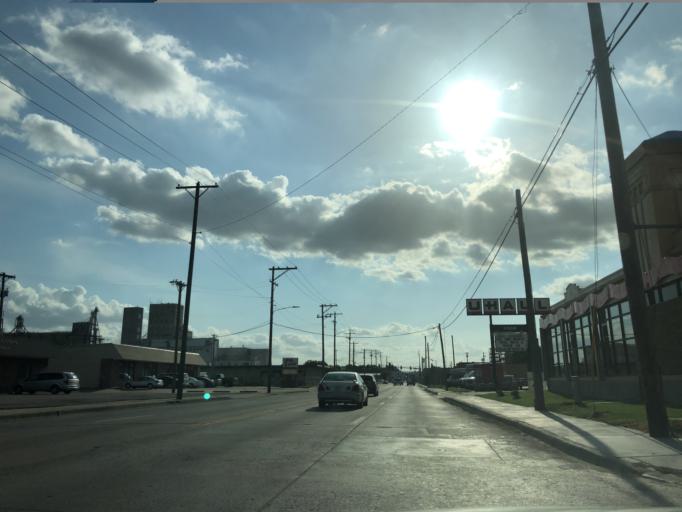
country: US
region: Kansas
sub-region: Sedgwick County
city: Wichita
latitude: 37.7081
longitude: -97.3252
